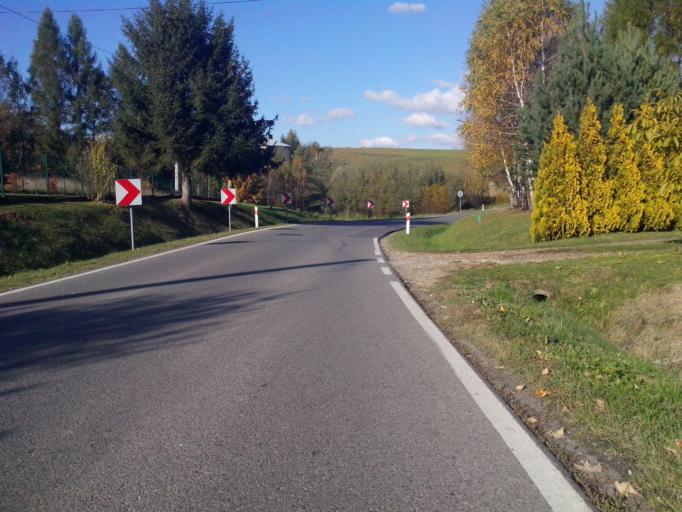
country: PL
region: Subcarpathian Voivodeship
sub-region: Powiat strzyzowski
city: Jawornik
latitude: 49.7926
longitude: 21.8588
